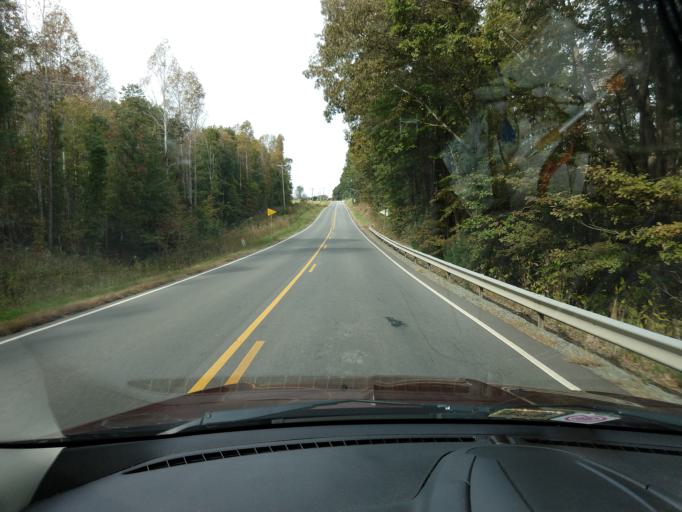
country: US
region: Virginia
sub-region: Franklin County
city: Union Hall
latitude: 36.9642
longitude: -79.5816
